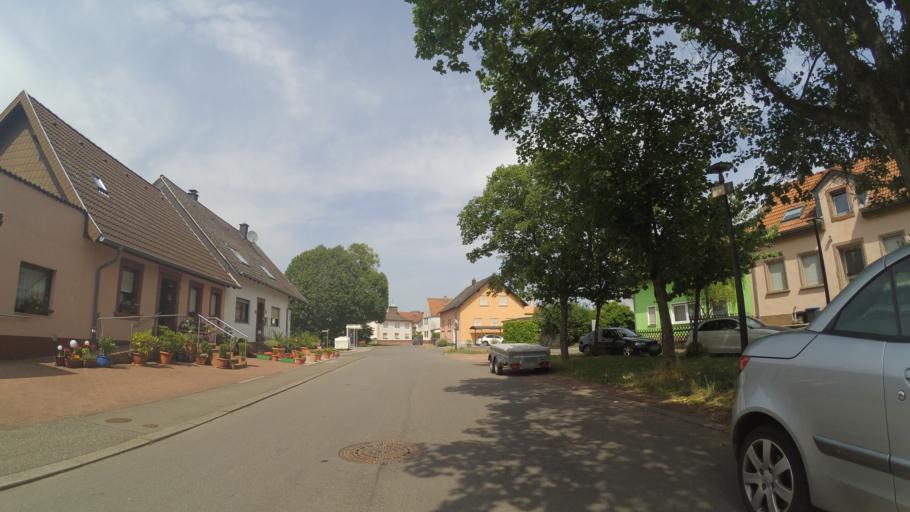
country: DE
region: Rheinland-Pfalz
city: Waldmohr
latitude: 49.3691
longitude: 7.3250
